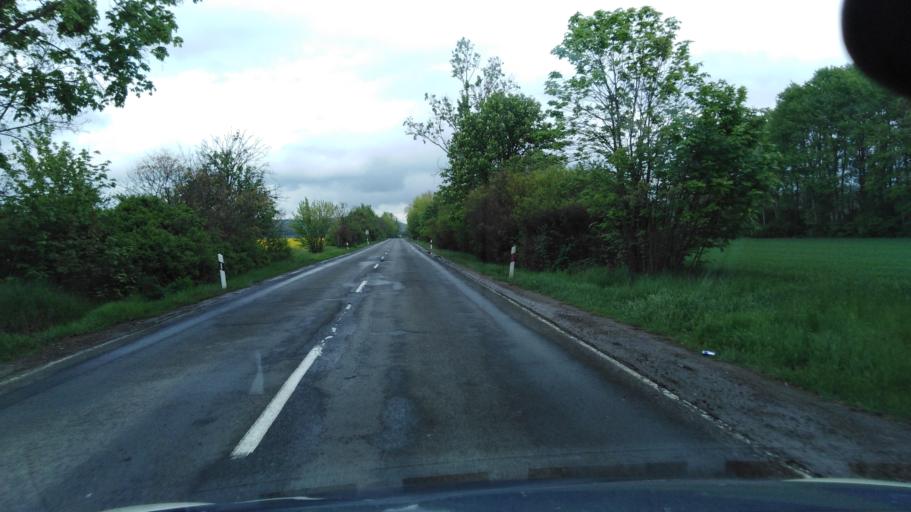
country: HU
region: Nograd
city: Szecseny
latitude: 48.1031
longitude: 19.5413
